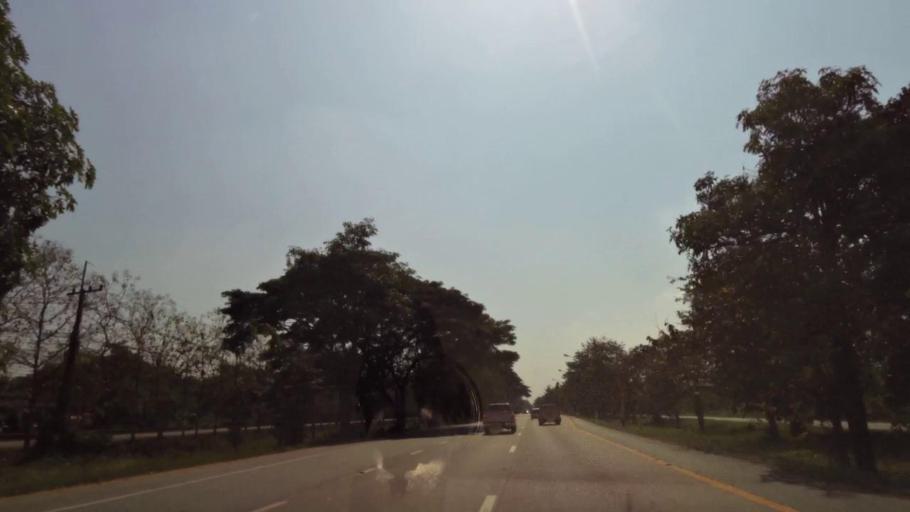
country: TH
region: Phichit
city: Wachira Barami
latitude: 16.5747
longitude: 100.1483
